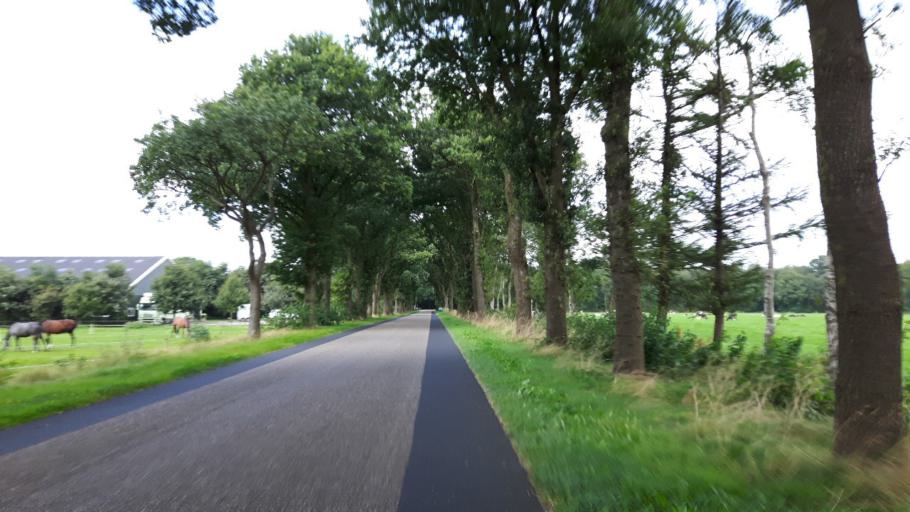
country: NL
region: Groningen
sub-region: Gemeente Leek
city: Leek
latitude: 53.0876
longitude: 6.3155
